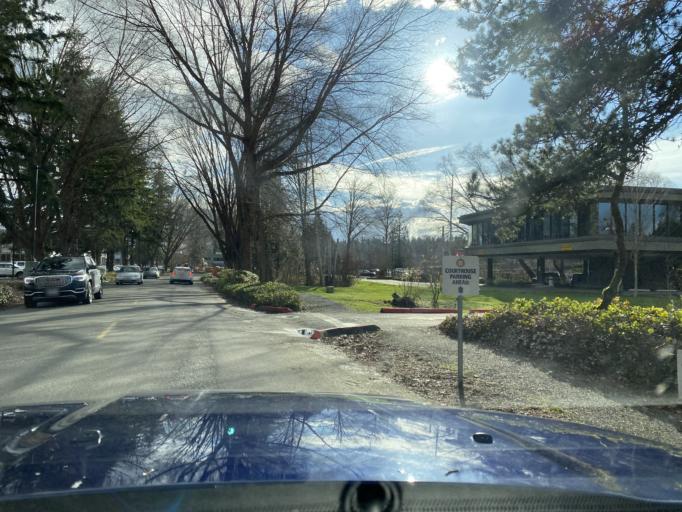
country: US
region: Washington
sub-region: King County
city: Bellevue
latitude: 47.5994
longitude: -122.1881
